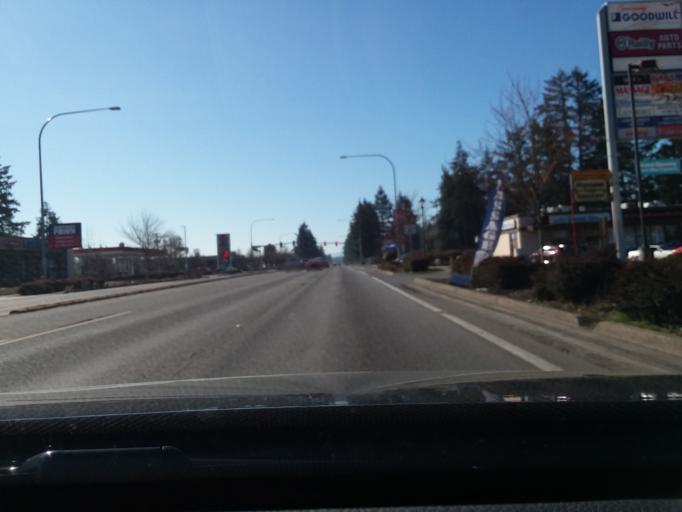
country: US
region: Washington
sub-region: Pierce County
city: Spanaway
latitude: 47.1207
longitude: -122.4350
